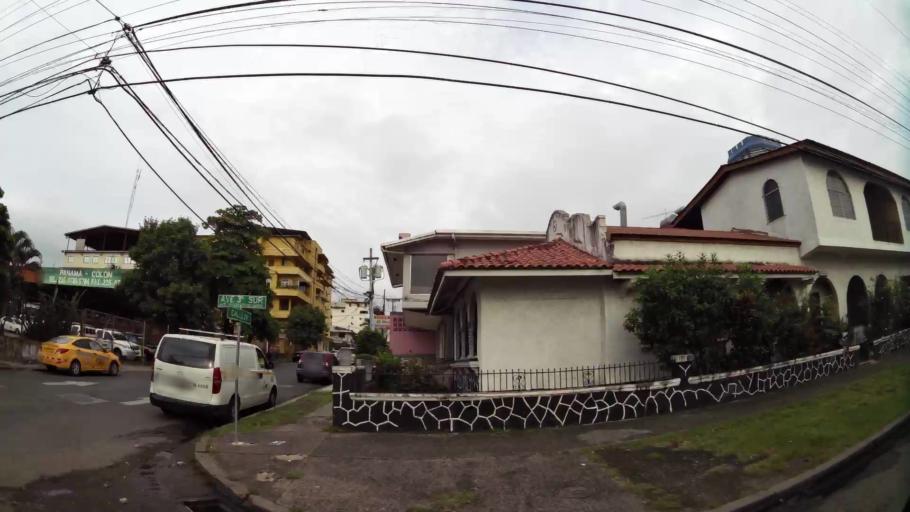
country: PA
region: Panama
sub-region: Distrito de Panama
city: Ancon
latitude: 8.9662
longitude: -79.5366
